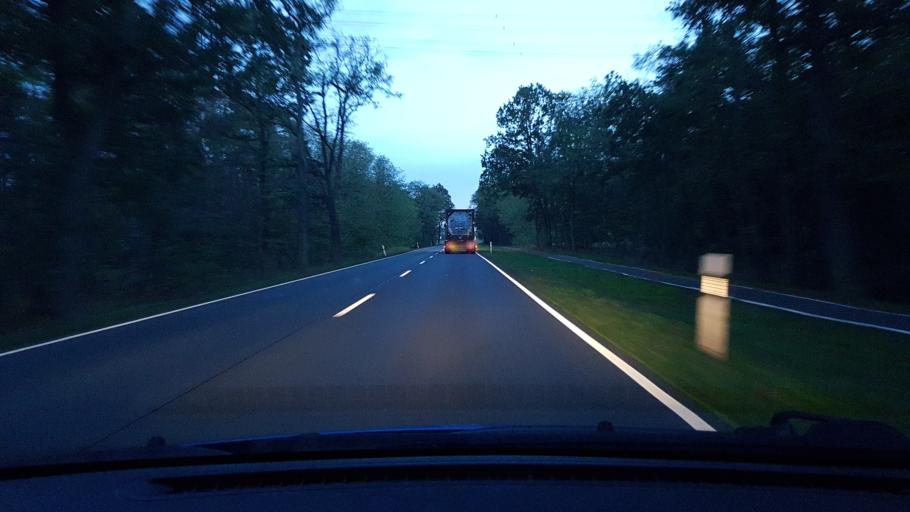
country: DE
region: Saxony-Anhalt
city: Zerbst
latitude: 51.9459
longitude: 12.1136
